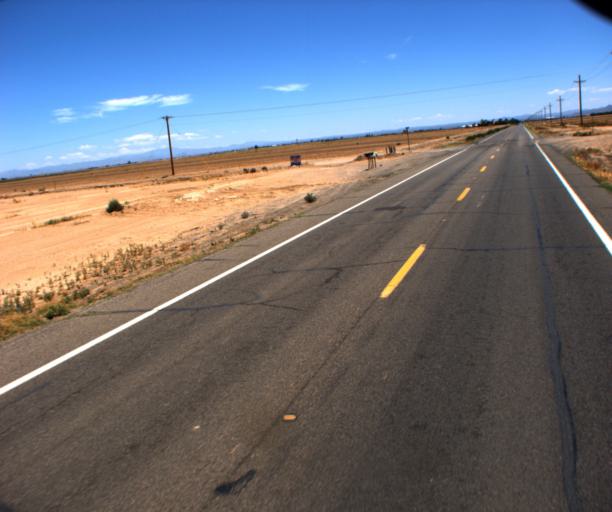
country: US
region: Arizona
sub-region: Pinal County
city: Coolidge
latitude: 32.8797
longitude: -111.6027
